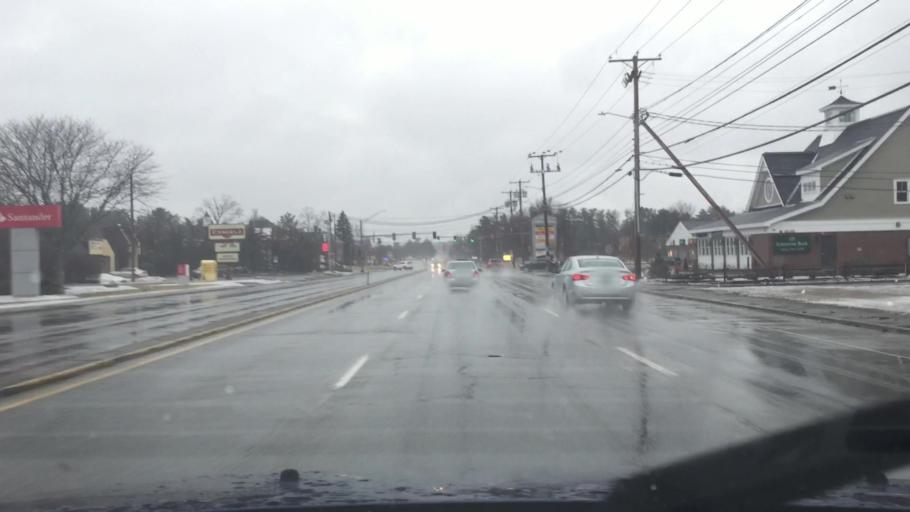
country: US
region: New Hampshire
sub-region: Hillsborough County
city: Nashua
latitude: 42.7921
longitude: -71.5215
